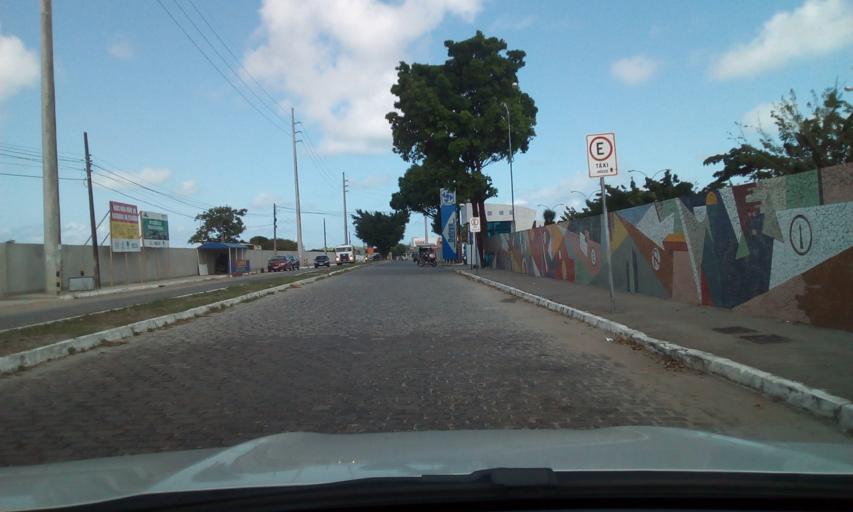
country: BR
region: Paraiba
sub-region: Joao Pessoa
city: Joao Pessoa
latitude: -7.1655
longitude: -34.8273
